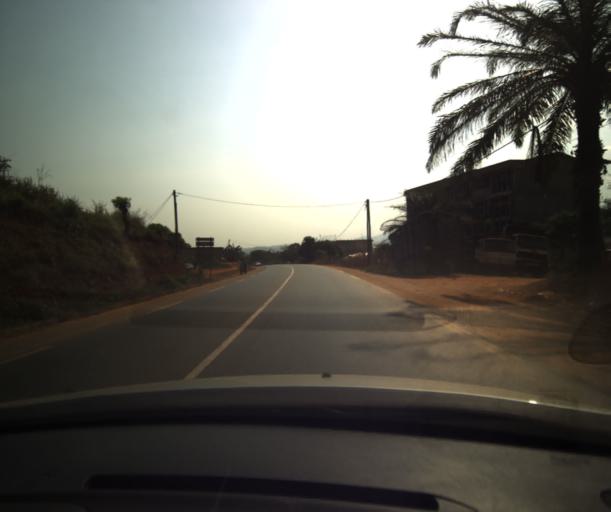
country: CM
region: Centre
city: Okoa
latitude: 3.9770
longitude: 11.5438
